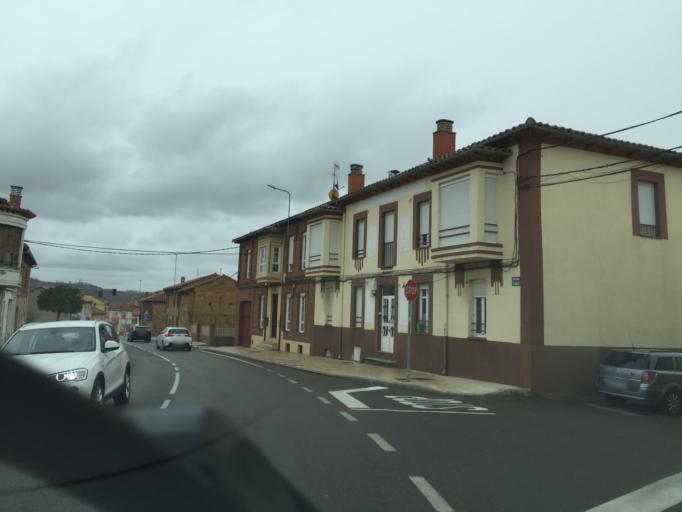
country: ES
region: Castille and Leon
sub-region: Provincia de Leon
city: Sariegos
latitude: 42.6693
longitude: -5.6338
